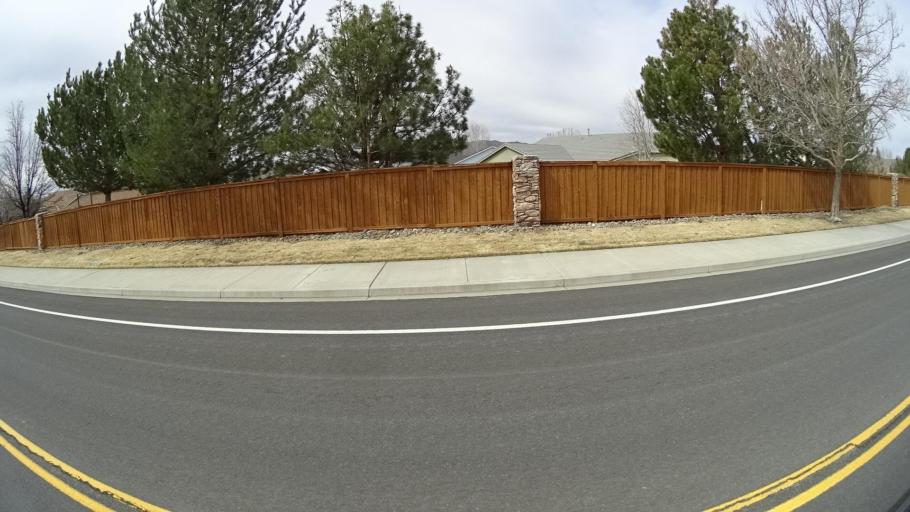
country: US
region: Nevada
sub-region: Washoe County
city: Spanish Springs
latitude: 39.6325
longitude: -119.6802
